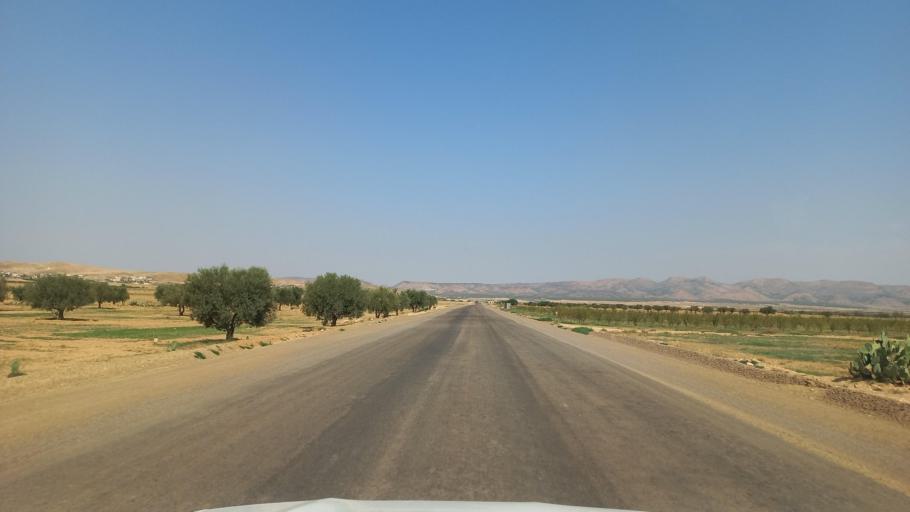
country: TN
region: Al Qasrayn
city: Sbiba
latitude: 35.3657
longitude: 9.0410
